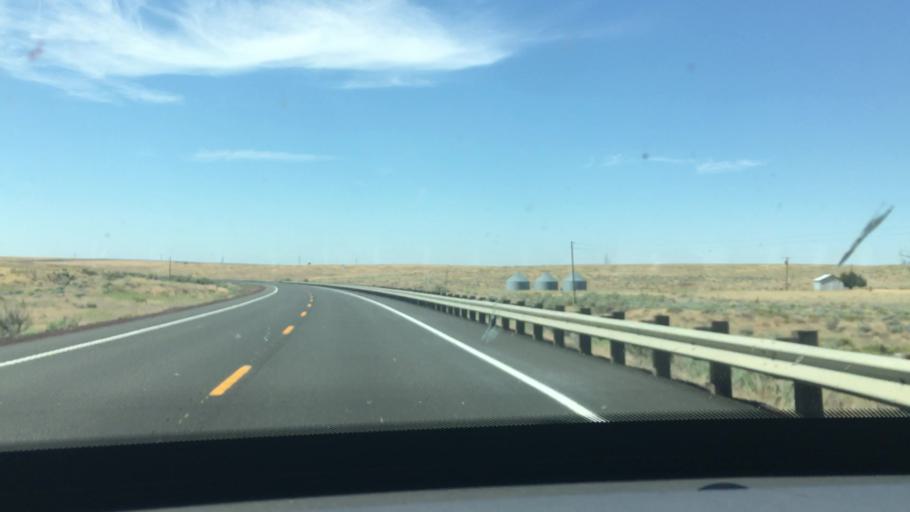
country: US
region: Oregon
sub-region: Sherman County
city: Moro
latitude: 45.2479
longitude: -120.7259
